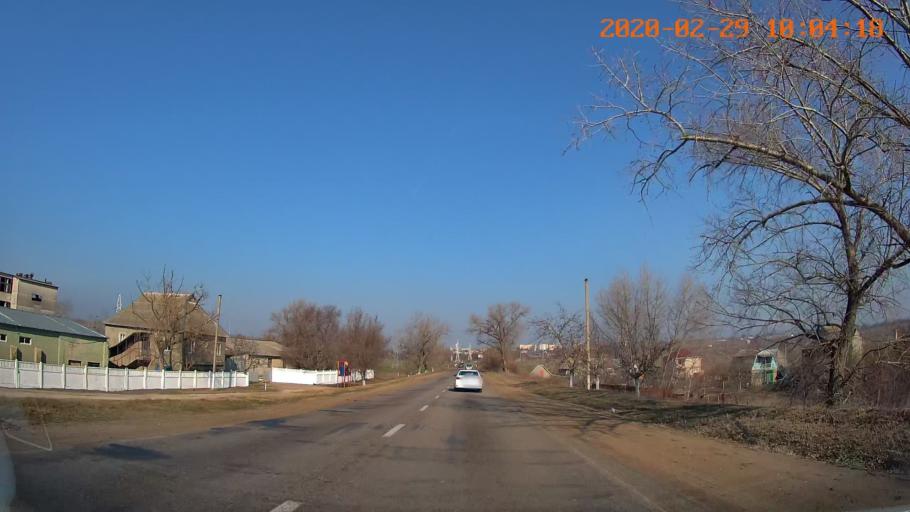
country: MD
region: Causeni
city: Chitcani
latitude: 46.7971
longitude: 29.6762
